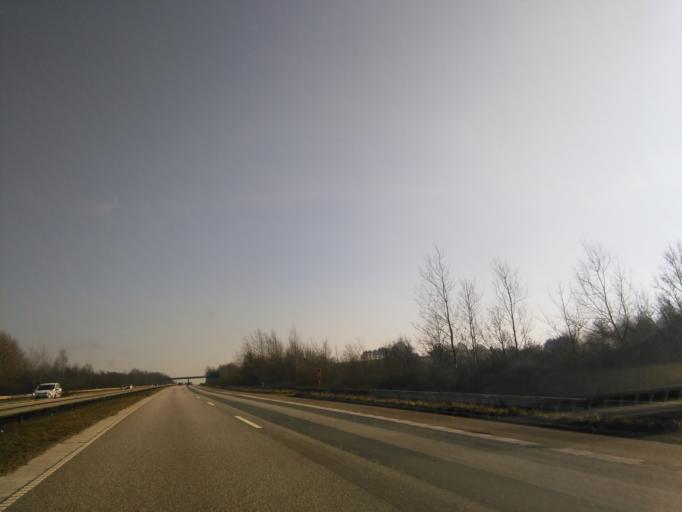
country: DK
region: South Denmark
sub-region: Assens Kommune
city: Vissenbjerg
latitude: 55.4068
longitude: 10.1329
